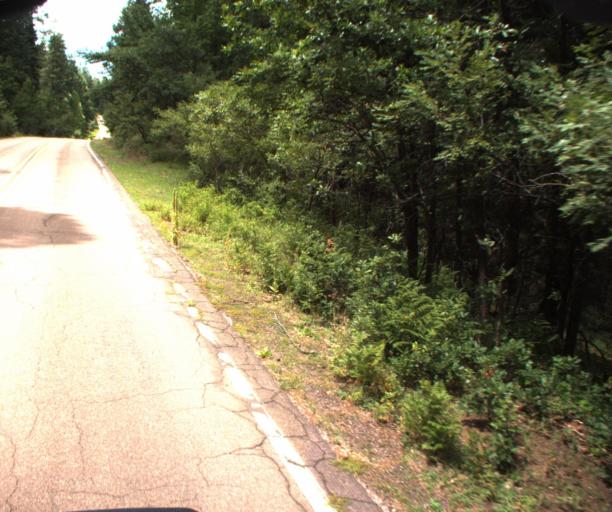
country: US
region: Arizona
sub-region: Navajo County
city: Pinetop-Lakeside
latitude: 34.0298
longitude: -109.7537
